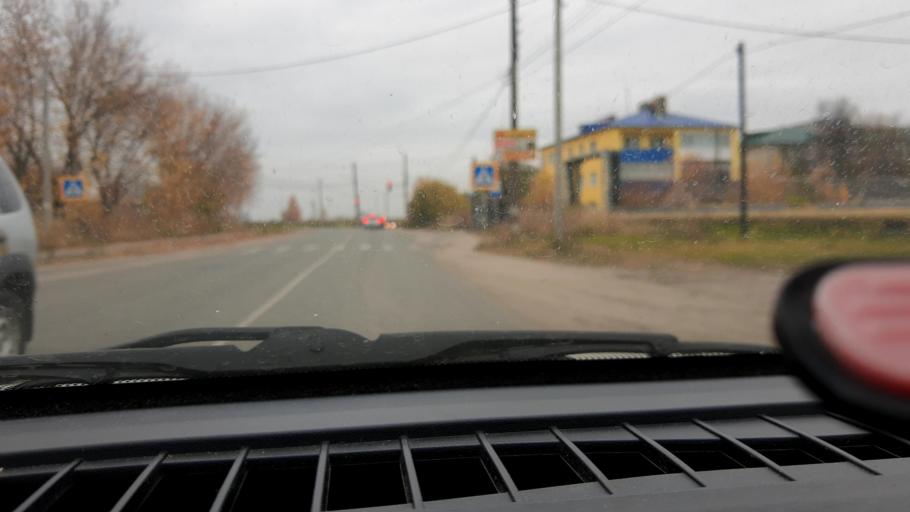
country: RU
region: Nizjnij Novgorod
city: Gorodets
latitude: 56.6412
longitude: 43.4897
